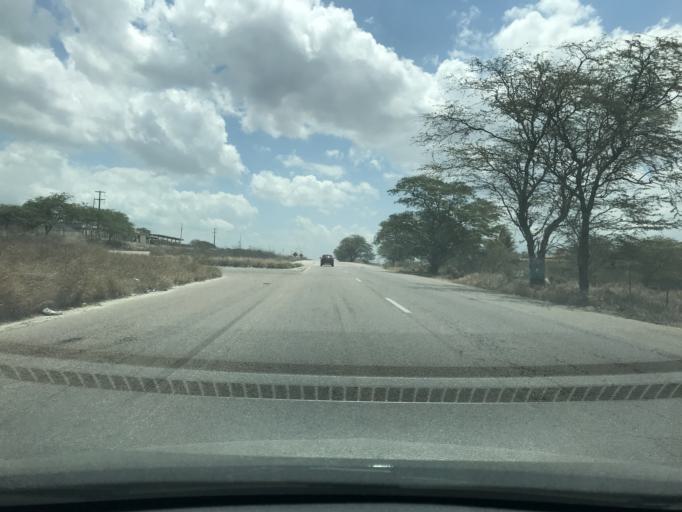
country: BR
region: Pernambuco
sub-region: Caruaru
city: Caruaru
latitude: -8.2955
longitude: -35.8892
